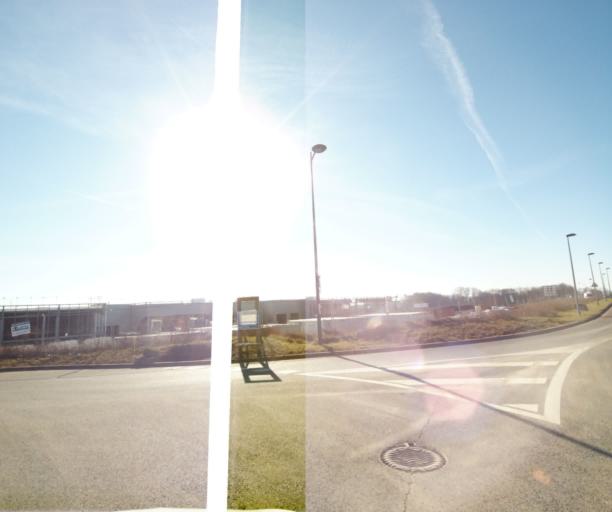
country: FR
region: Lorraine
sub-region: Departement de Meurthe-et-Moselle
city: Laxou
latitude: 48.7074
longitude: 6.1360
